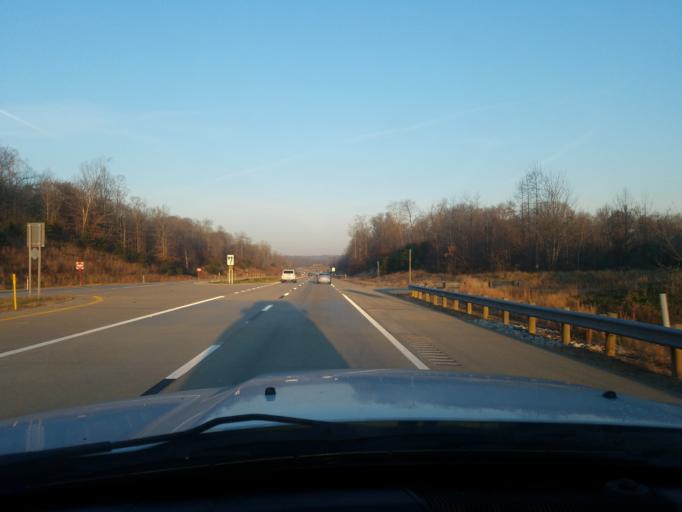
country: US
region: West Virginia
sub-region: Putnam County
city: Eleanor
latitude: 38.5399
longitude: -81.9636
